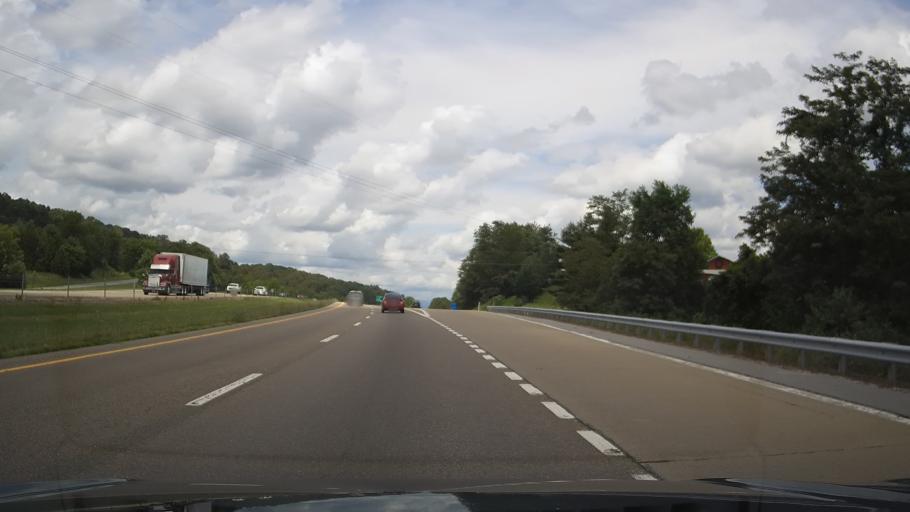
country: US
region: Tennessee
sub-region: Unicoi County
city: Unicoi
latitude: 36.2033
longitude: -82.3573
